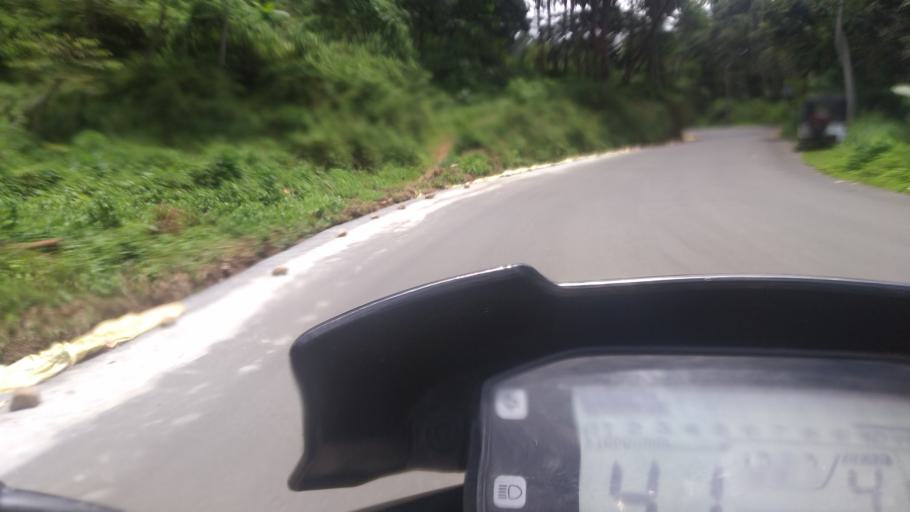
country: IN
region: Kerala
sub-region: Idukki
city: Munnar
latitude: 10.0386
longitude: 76.9979
